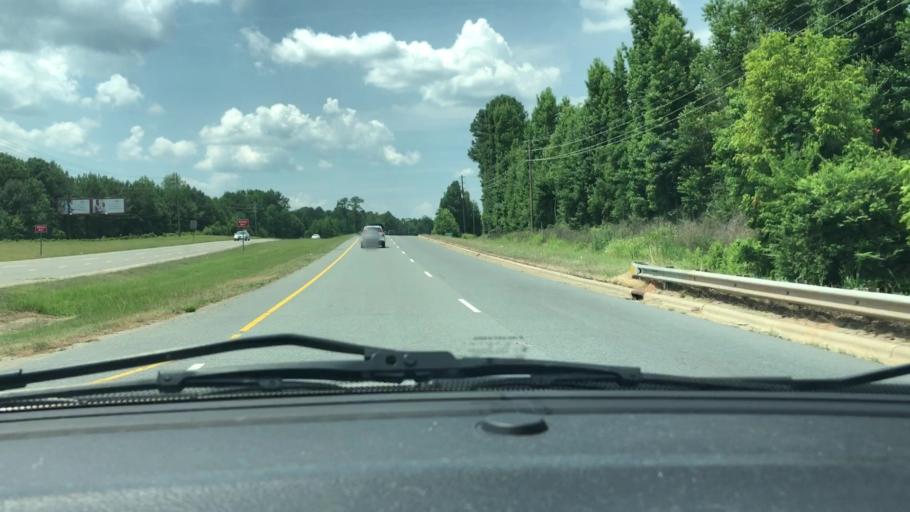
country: US
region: North Carolina
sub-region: Lee County
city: Sanford
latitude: 35.5004
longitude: -79.2028
